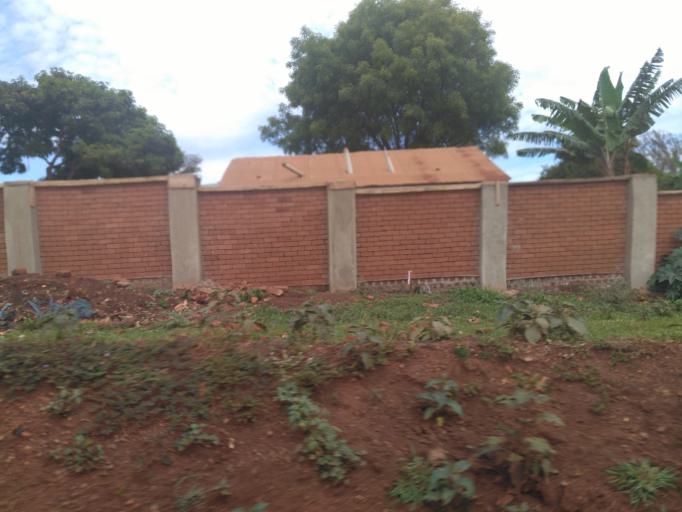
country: UG
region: Central Region
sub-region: Buikwe District
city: Njeru
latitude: 0.4256
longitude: 33.1900
